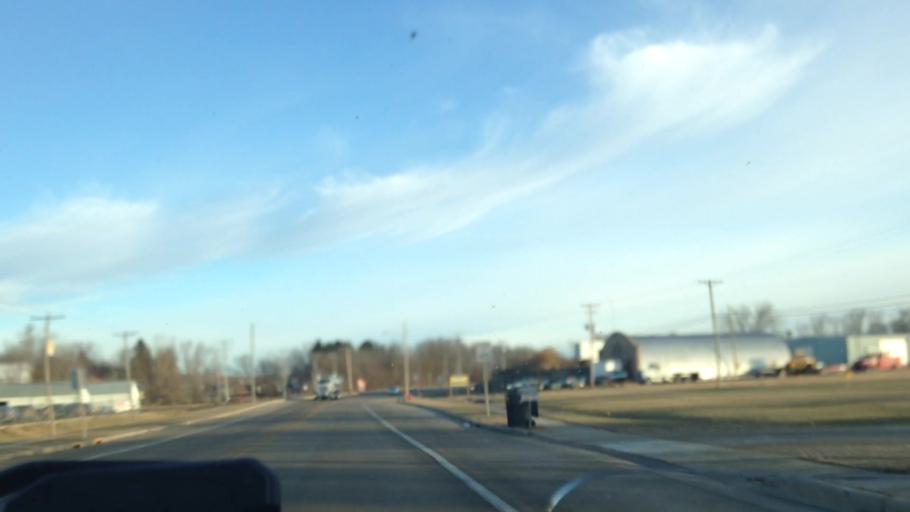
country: US
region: Wisconsin
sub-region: Dodge County
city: Mayville
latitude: 43.5074
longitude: -88.5419
